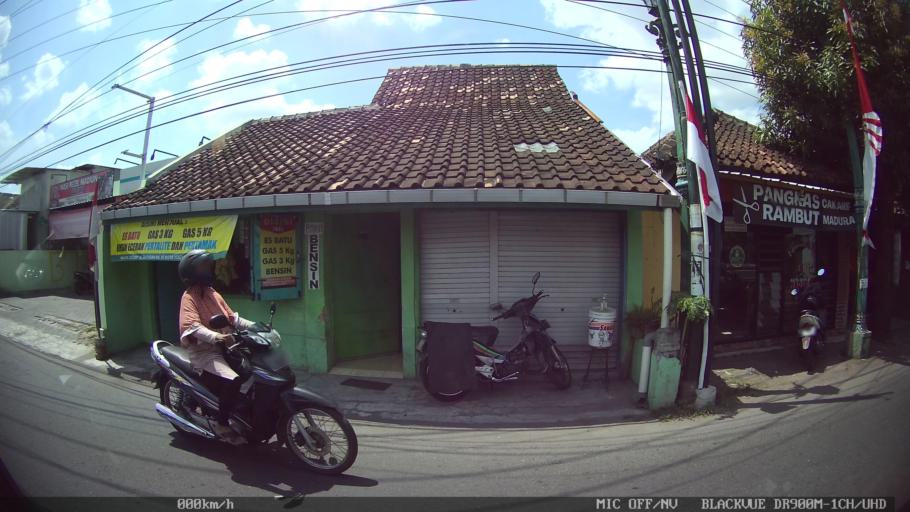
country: ID
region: Daerah Istimewa Yogyakarta
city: Kasihan
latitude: -7.8128
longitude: 110.3493
